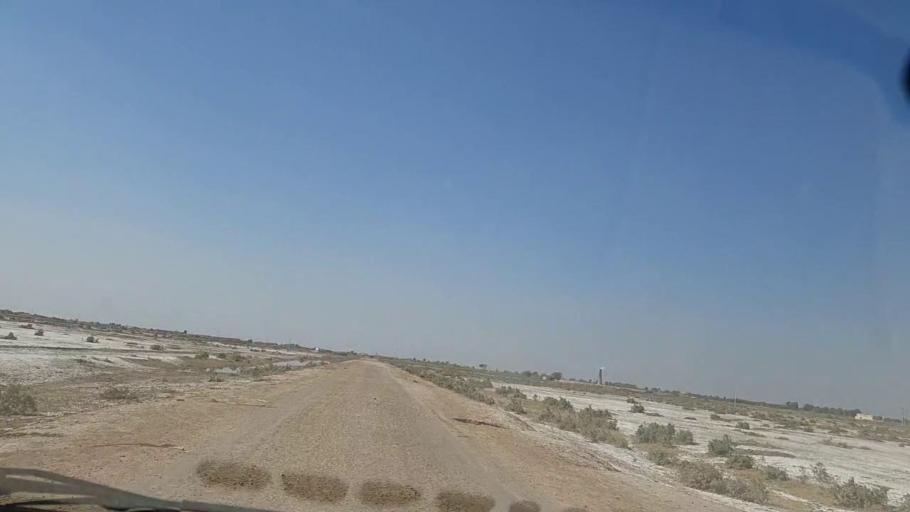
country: PK
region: Sindh
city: Mirwah Gorchani
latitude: 25.3762
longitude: 69.0116
